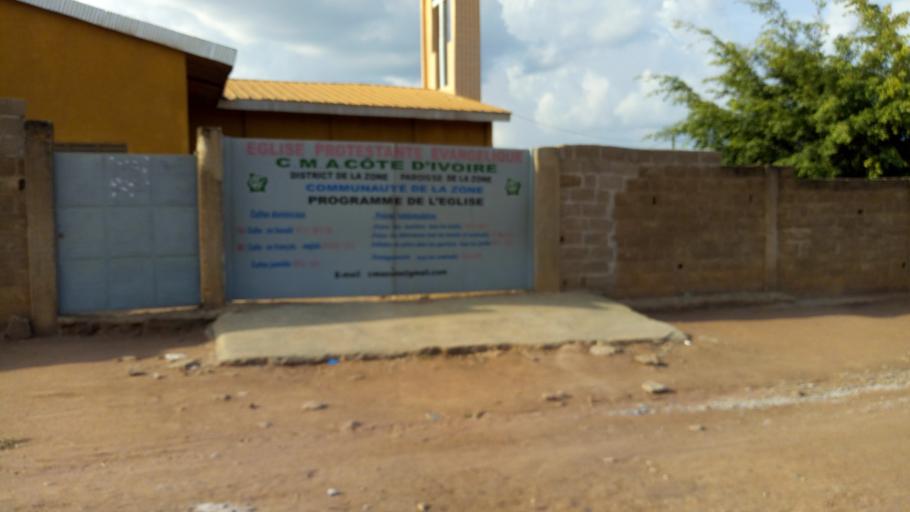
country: CI
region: Vallee du Bandama
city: Bouake
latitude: 7.7044
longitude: -5.0581
